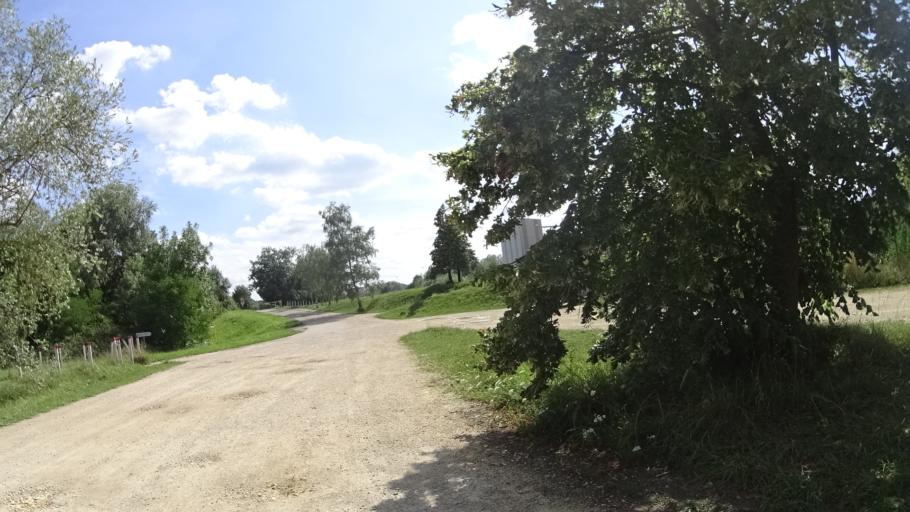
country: FR
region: Lorraine
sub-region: Departement de Meurthe-et-Moselle
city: Toul
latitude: 48.6700
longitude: 5.8949
